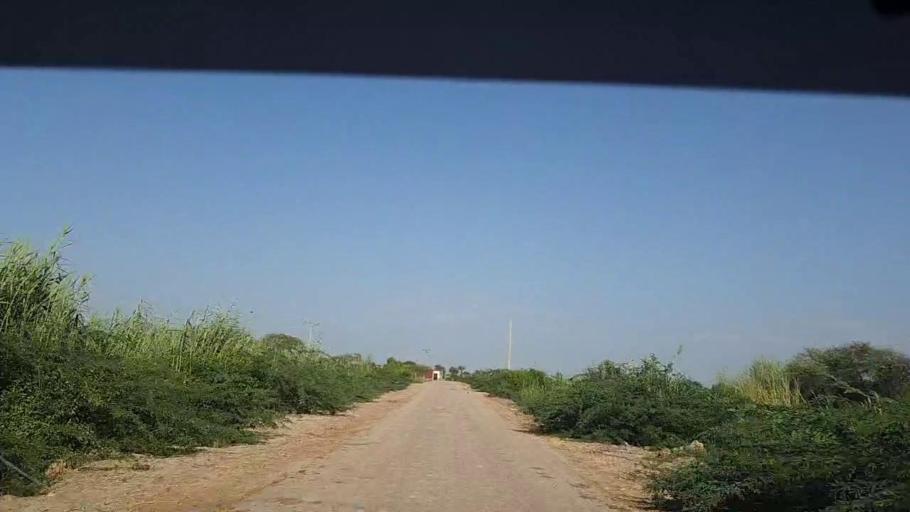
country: PK
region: Sindh
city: Kadhan
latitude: 24.4639
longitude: 68.8499
